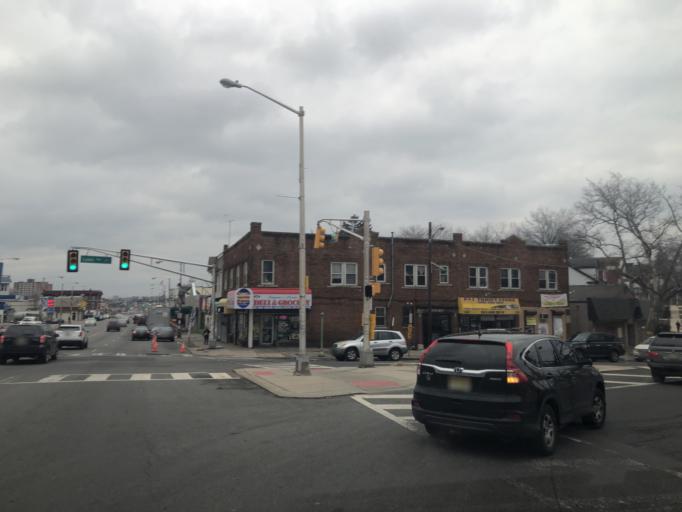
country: US
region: New Jersey
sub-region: Essex County
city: Irvington
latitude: 40.7249
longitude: -74.2398
